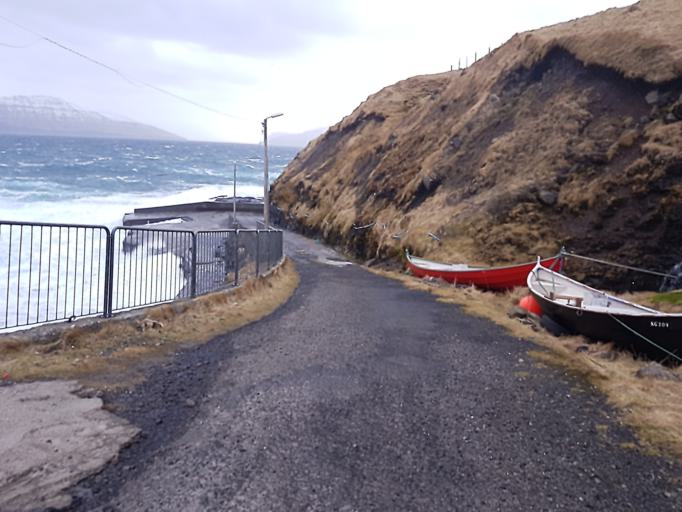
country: FO
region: Nordoyar
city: Klaksvik
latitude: 62.3547
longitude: -6.5190
